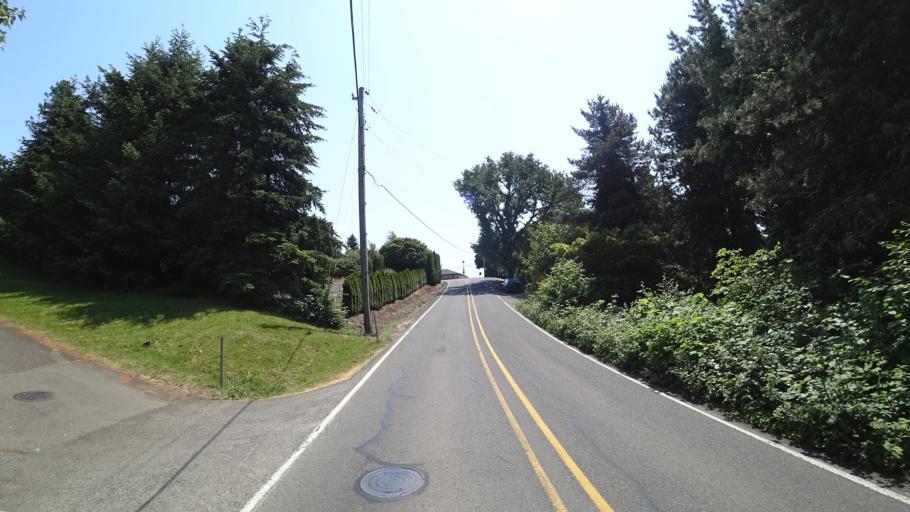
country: US
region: Oregon
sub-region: Clackamas County
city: Happy Valley
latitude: 45.4476
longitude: -122.5515
